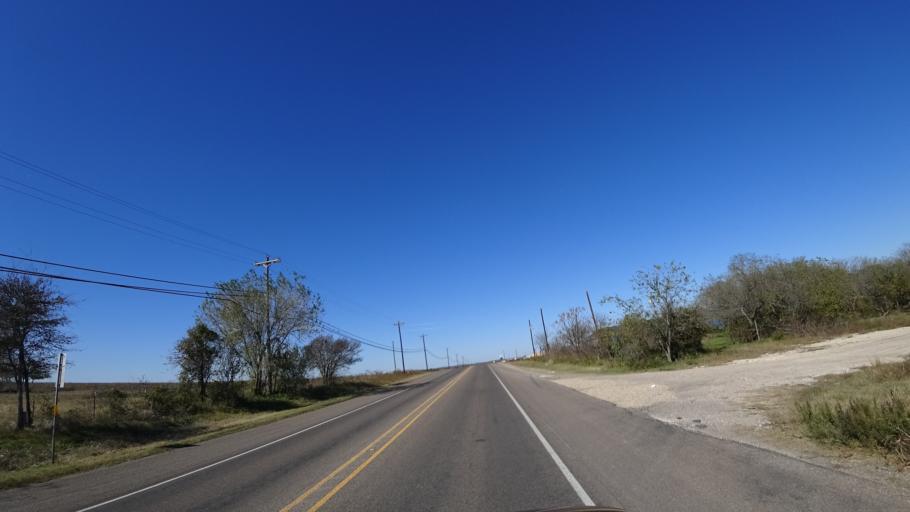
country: US
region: Texas
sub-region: Travis County
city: Garfield
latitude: 30.0987
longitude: -97.6043
